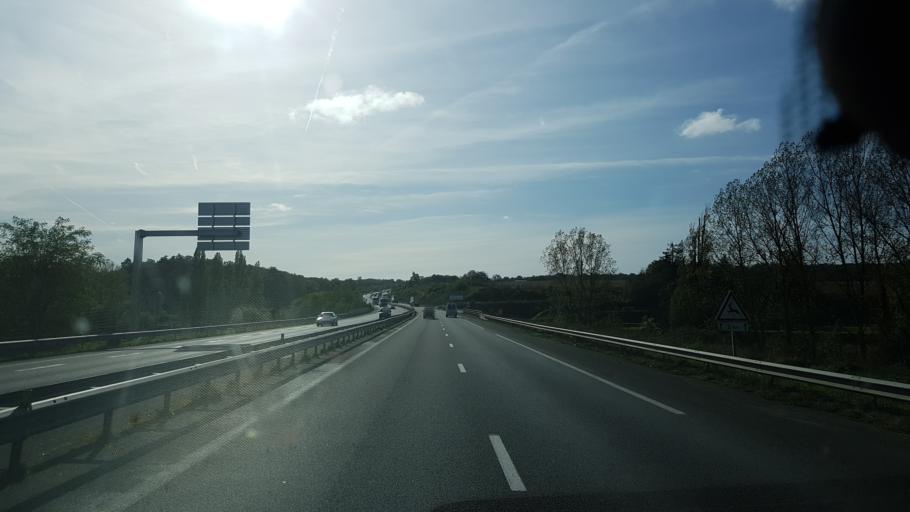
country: FR
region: Poitou-Charentes
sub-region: Departement de la Charente
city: Saint-Projet-Saint-Constant
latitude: 45.7360
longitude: 0.3415
